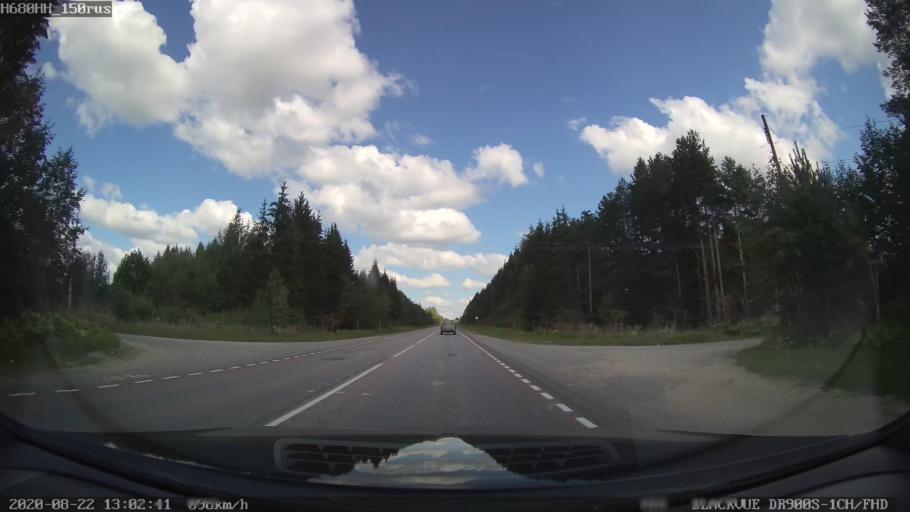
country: RU
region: Tverskaya
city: Bezhetsk
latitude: 57.6518
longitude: 36.4003
